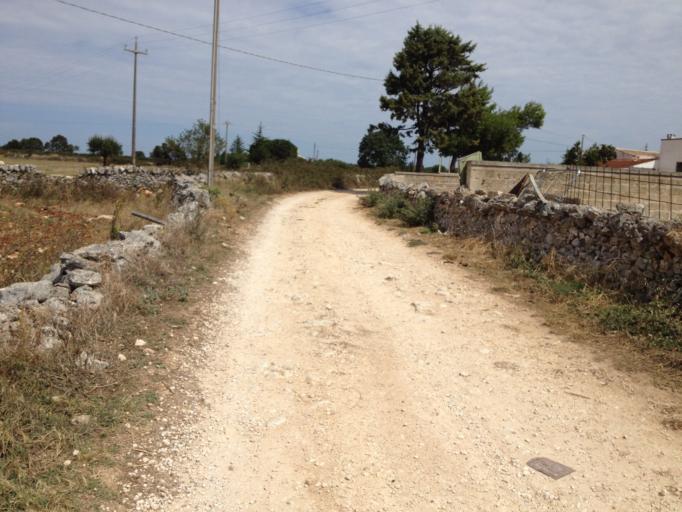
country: IT
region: Apulia
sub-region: Provincia di Bari
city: Gioia del Colle
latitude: 40.8242
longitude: 16.9793
